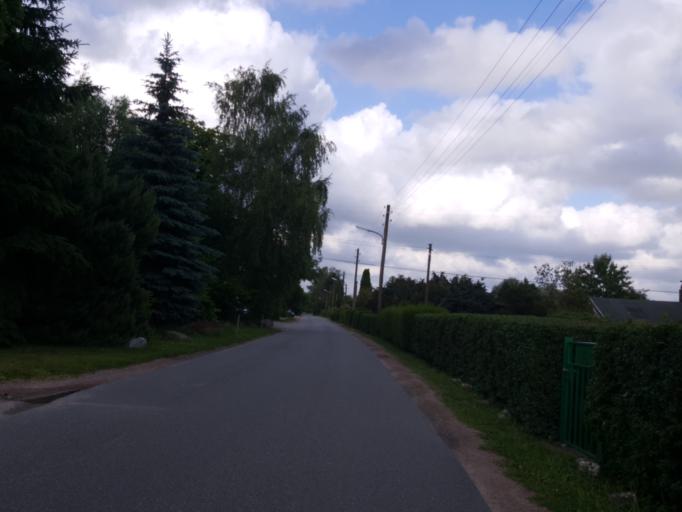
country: DE
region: Hamburg
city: Marienthal
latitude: 53.5385
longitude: 10.0764
